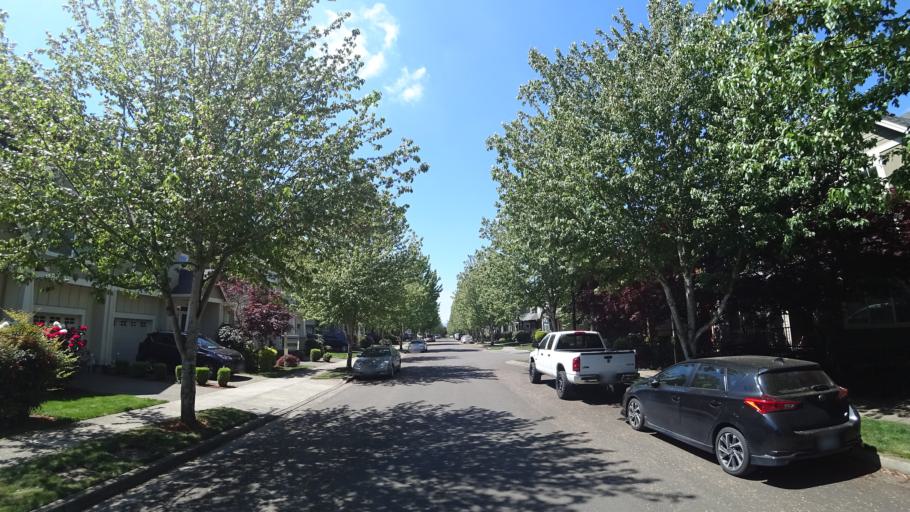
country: US
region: Oregon
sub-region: Washington County
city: Hillsboro
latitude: 45.5074
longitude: -122.9721
